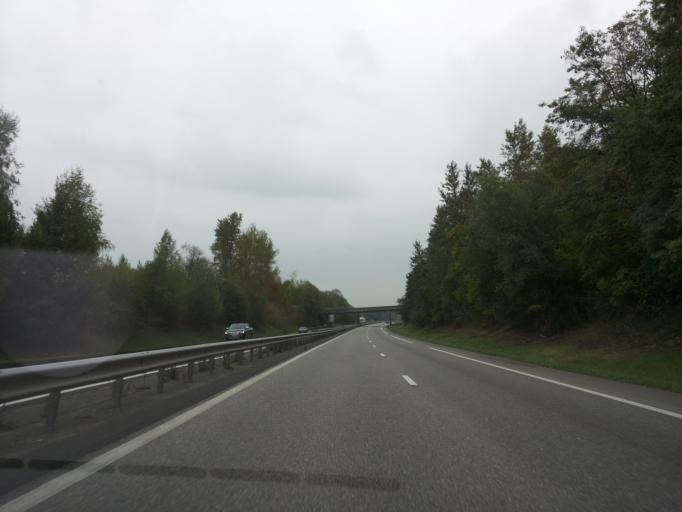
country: FR
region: Lorraine
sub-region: Departement de la Moselle
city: Sarrebourg
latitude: 48.7265
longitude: 7.0643
